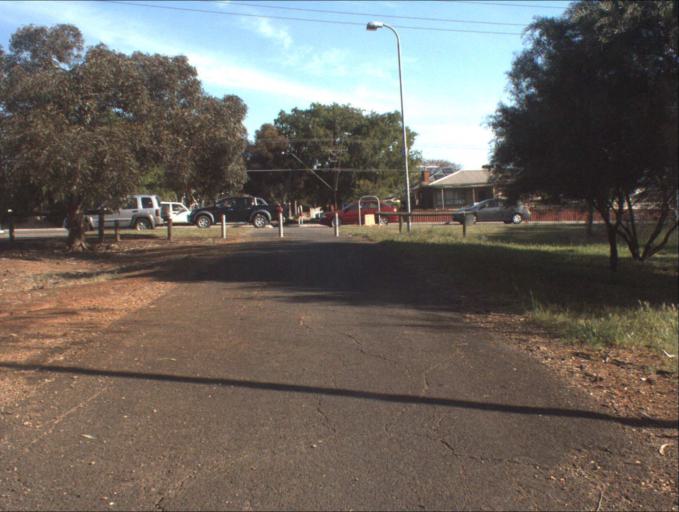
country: AU
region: South Australia
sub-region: Port Adelaide Enfield
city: Enfield
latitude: -34.8470
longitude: 138.6137
